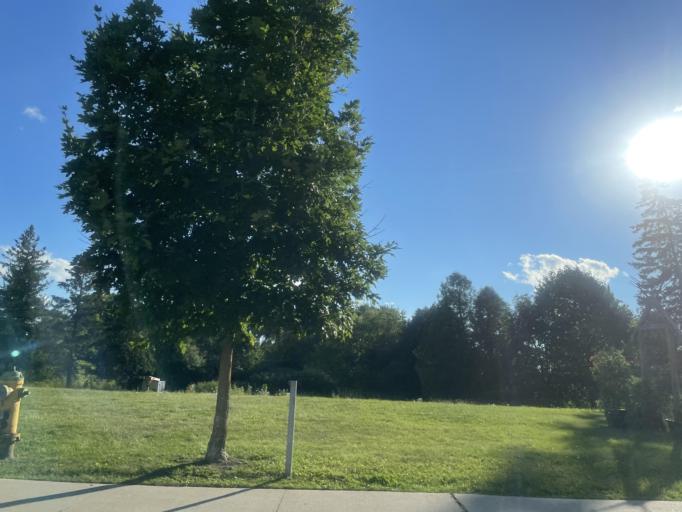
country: CA
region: Ontario
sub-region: Wellington County
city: Guelph
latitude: 43.5493
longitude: -80.2687
